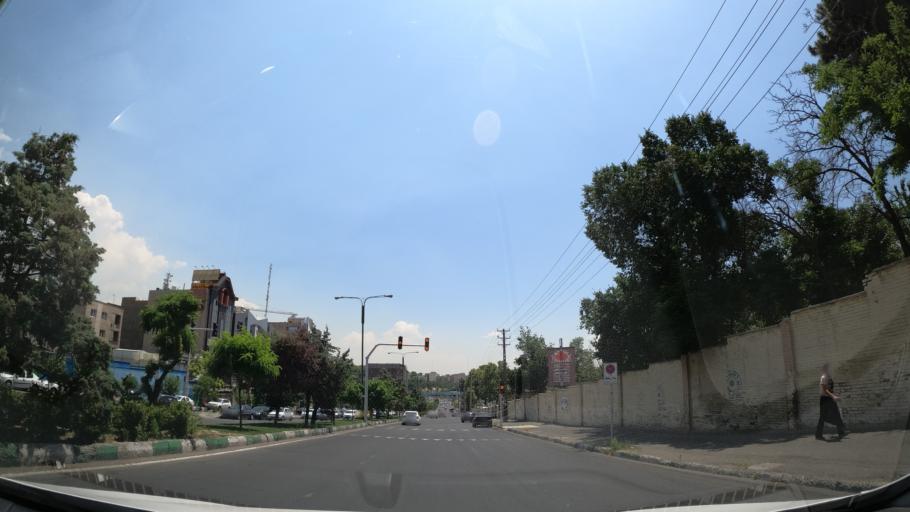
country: IR
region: Tehran
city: Tajrish
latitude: 35.7708
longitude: 51.3819
